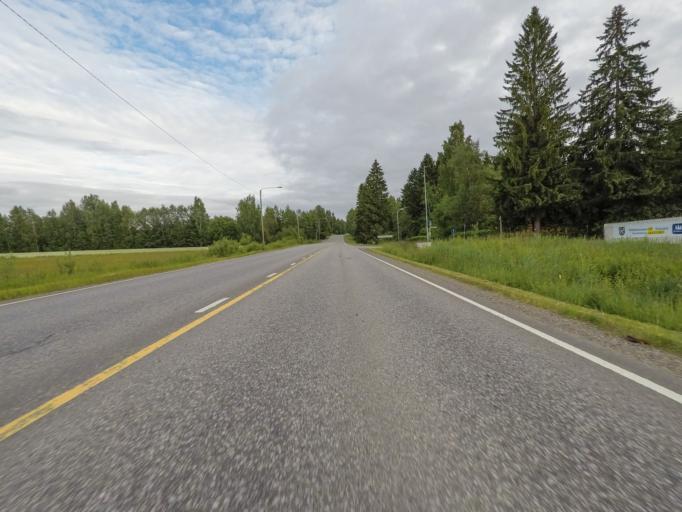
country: FI
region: Southern Savonia
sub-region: Savonlinna
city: Savonlinna
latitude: 61.8831
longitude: 28.9413
